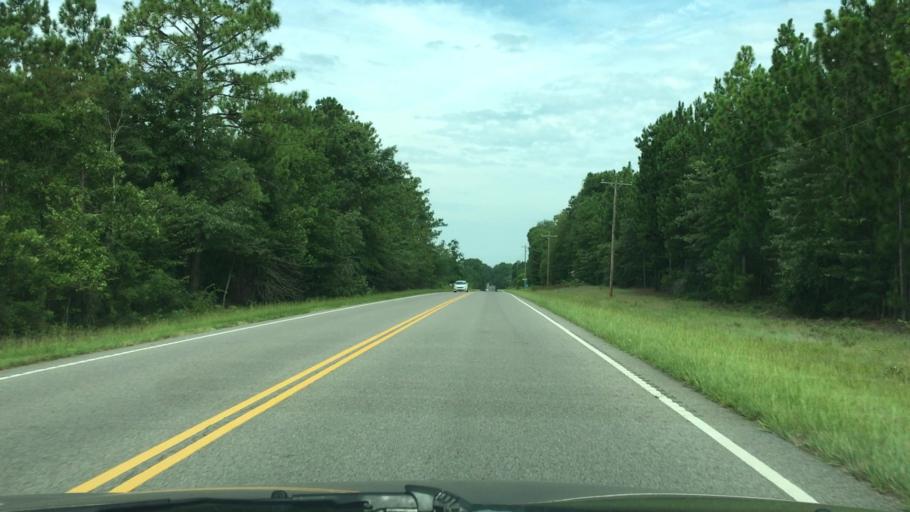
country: US
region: South Carolina
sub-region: Lexington County
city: Leesville
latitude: 33.6739
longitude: -81.4223
